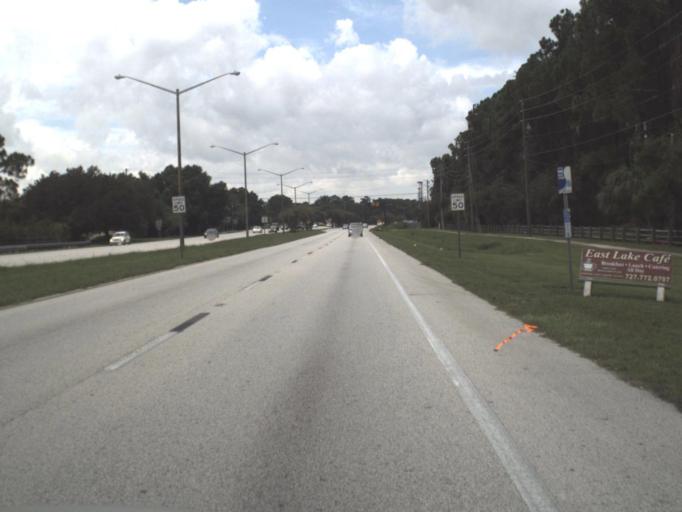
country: US
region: Florida
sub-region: Pinellas County
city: East Lake
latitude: 28.0879
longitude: -82.6995
